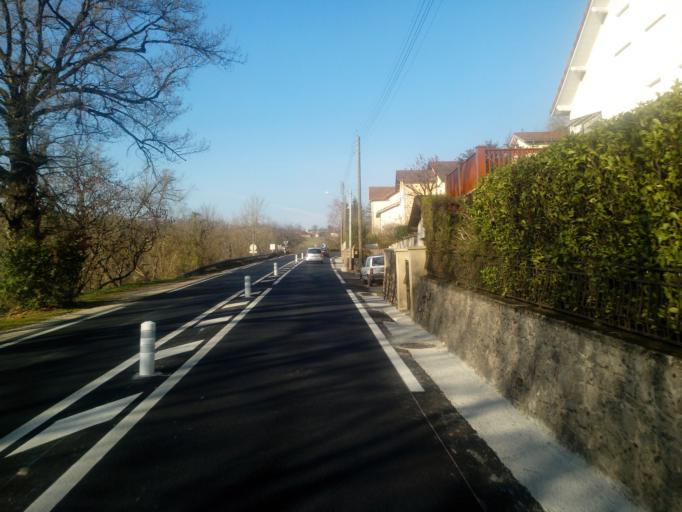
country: FR
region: Midi-Pyrenees
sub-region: Departement de l'Aveyron
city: Capdenac-Gare
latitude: 44.5810
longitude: 2.0666
